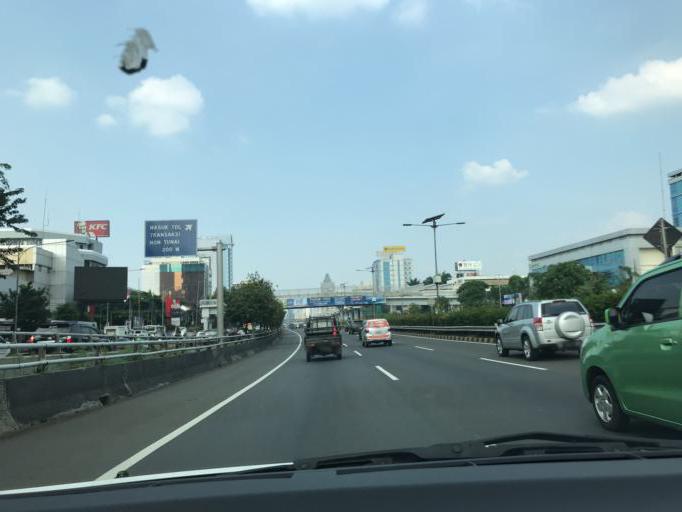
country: ID
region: Jakarta Raya
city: Jakarta
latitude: -6.2434
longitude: 106.8458
